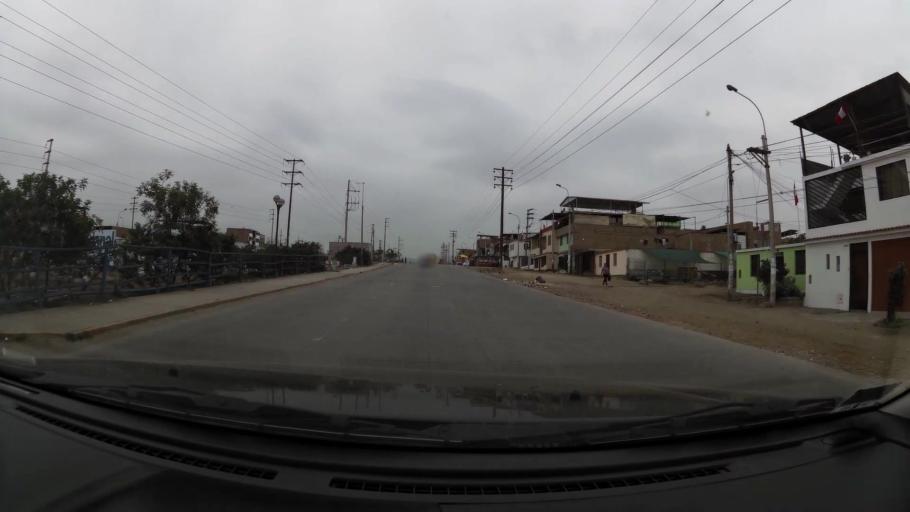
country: PE
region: Lima
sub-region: Lima
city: Surco
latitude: -12.2031
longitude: -76.9481
